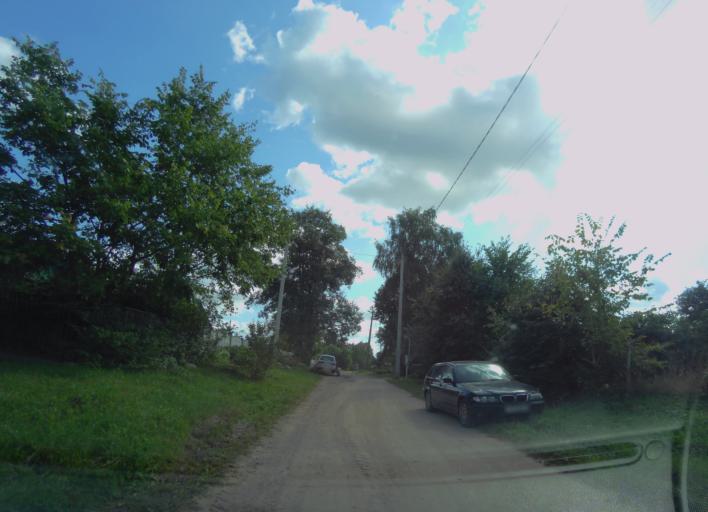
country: BY
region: Minsk
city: Zyembin
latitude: 54.3775
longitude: 28.3698
